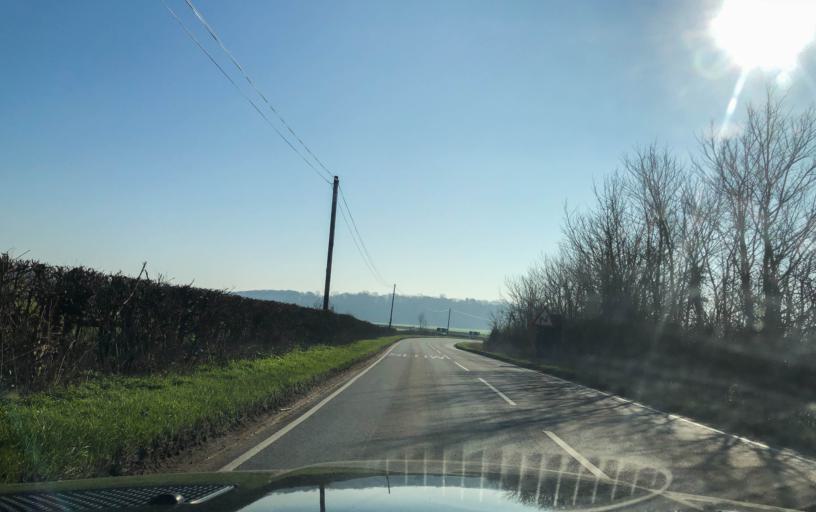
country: GB
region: England
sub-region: Warwickshire
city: Wellesbourne Mountford
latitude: 52.1875
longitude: -1.5814
